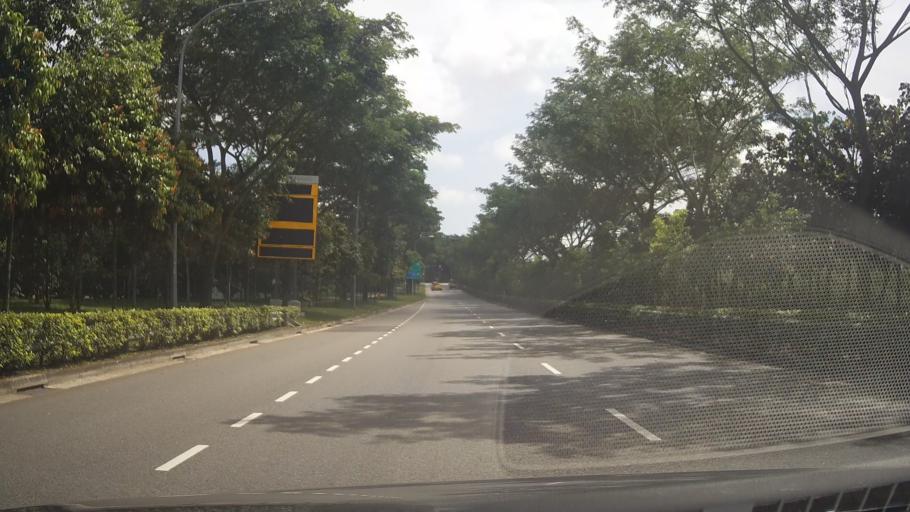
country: MY
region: Johor
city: Kampung Pasir Gudang Baru
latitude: 1.4015
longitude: 103.8698
